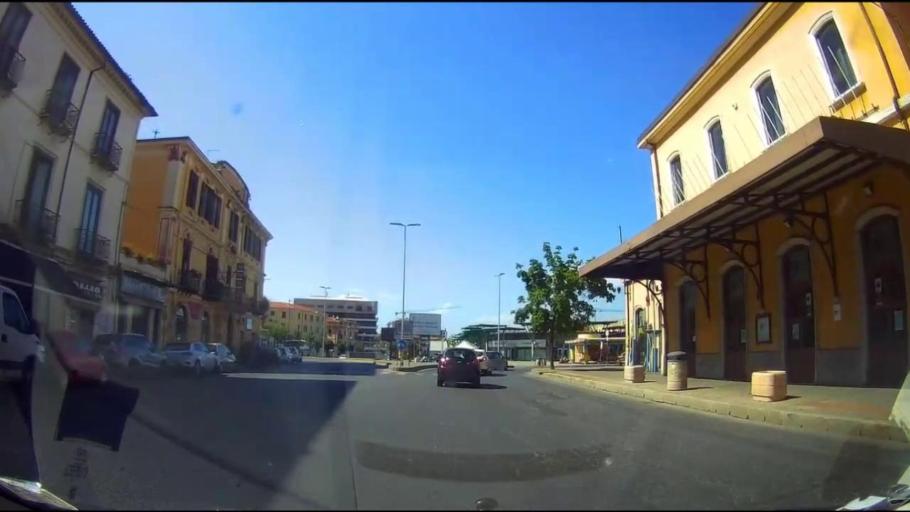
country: IT
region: Calabria
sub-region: Provincia di Cosenza
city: Cosenza
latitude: 39.2940
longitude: 16.2567
